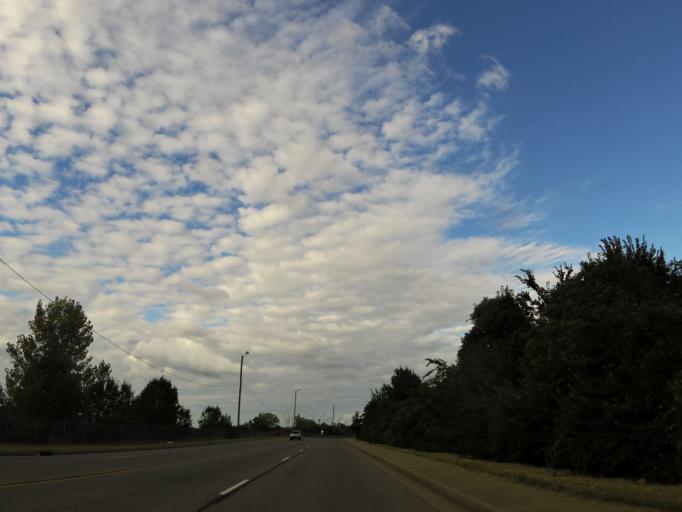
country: US
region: Tennessee
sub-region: Davidson County
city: Nashville
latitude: 36.1707
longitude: -86.8321
